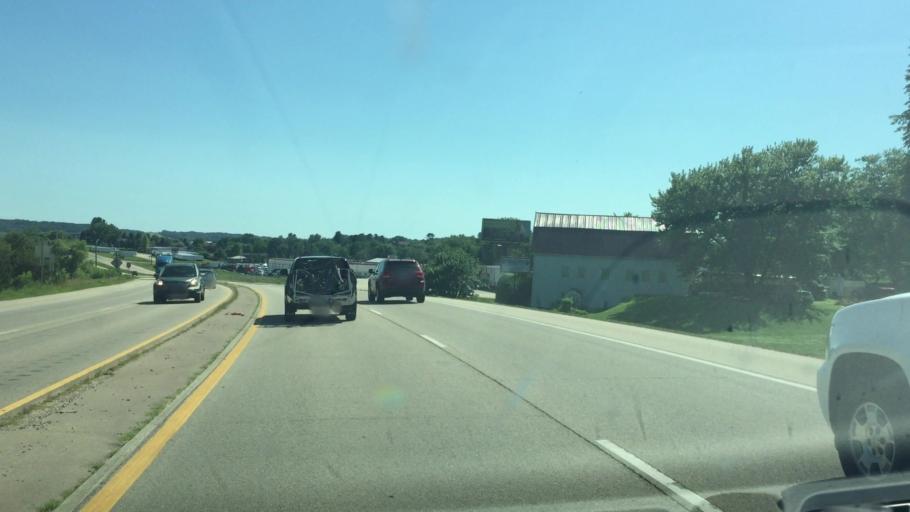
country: US
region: Iowa
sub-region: Dubuque County
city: Dubuque
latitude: 42.4535
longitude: -90.6789
